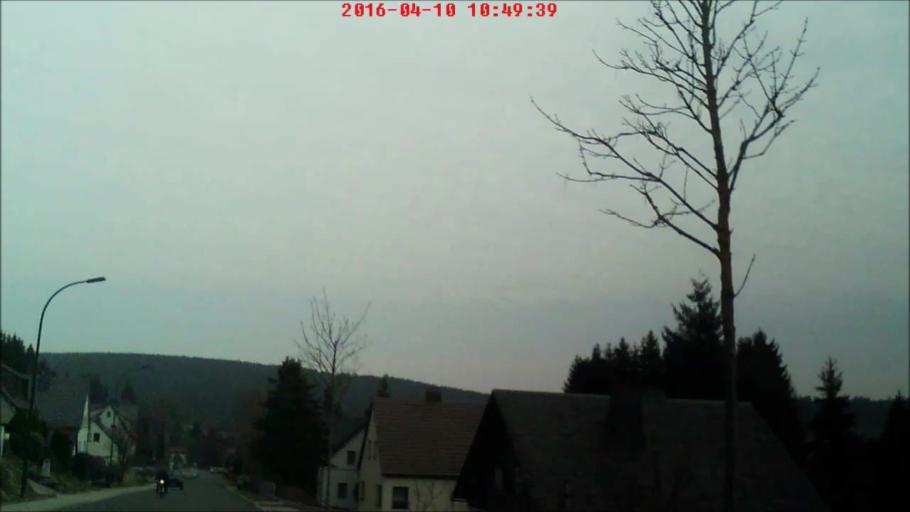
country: DE
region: Thuringia
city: Schmiedefeld am Rennsteig
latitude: 50.6290
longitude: 10.8479
